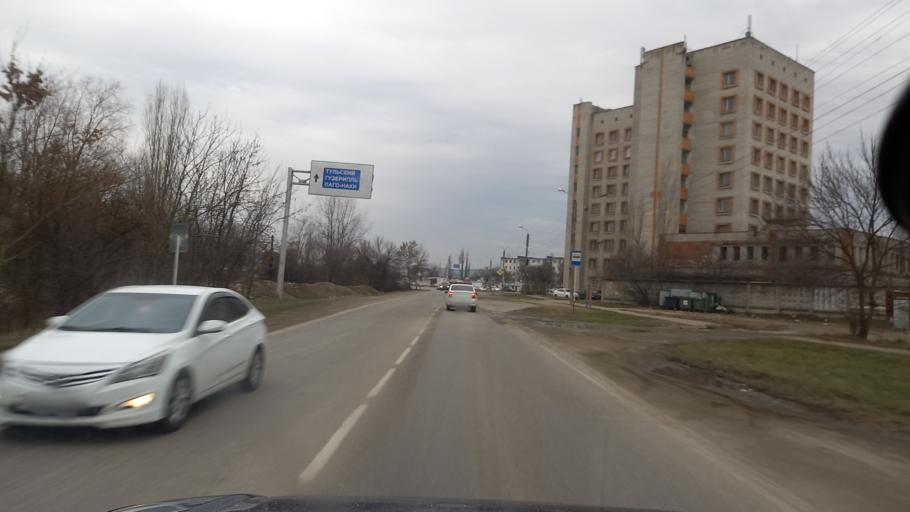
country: RU
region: Adygeya
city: Maykop
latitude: 44.5764
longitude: 40.1346
